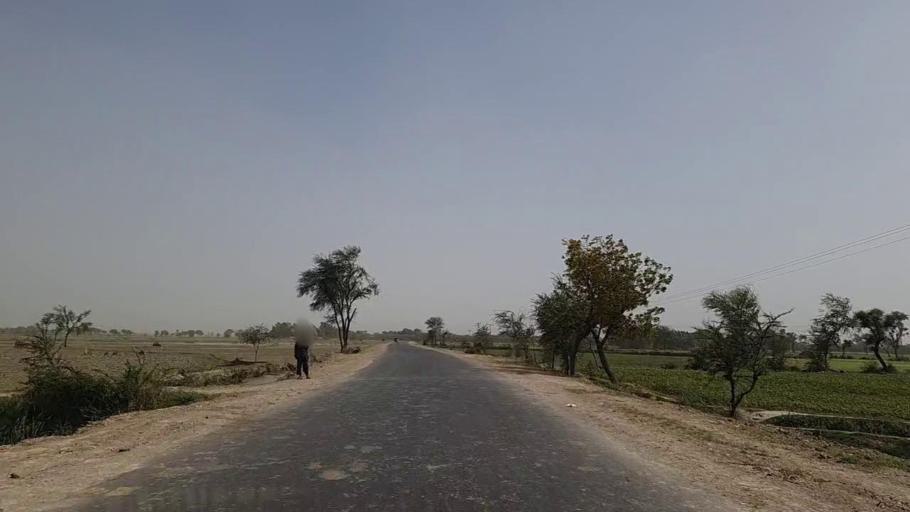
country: PK
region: Sindh
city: Tando Bago
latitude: 24.8131
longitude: 68.9111
